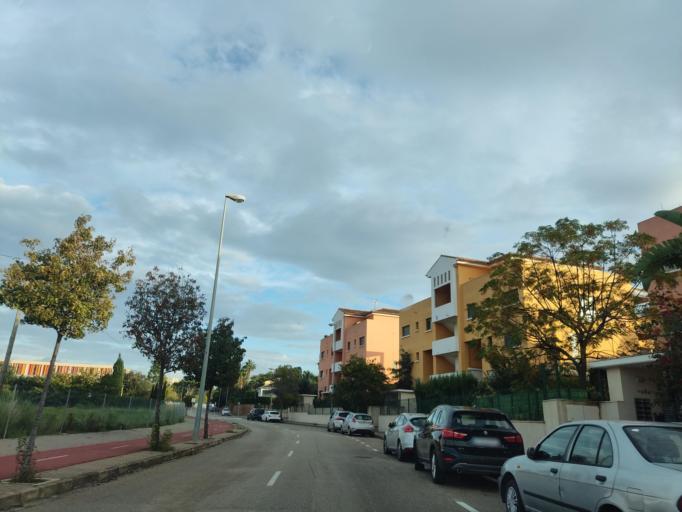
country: ES
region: Valencia
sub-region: Provincia de Alicante
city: Denia
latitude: 38.8332
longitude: 0.1121
